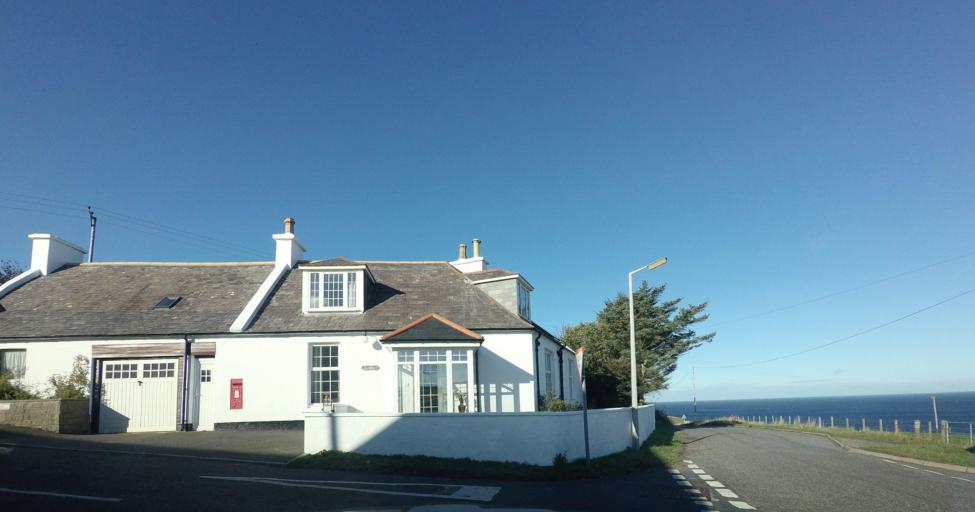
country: GB
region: Scotland
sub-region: Aberdeenshire
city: Rosehearty
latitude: 57.6764
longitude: -2.2620
